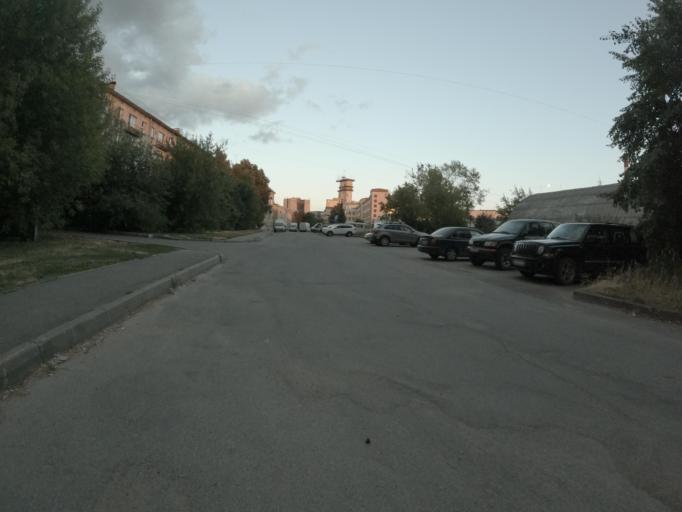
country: RU
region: St.-Petersburg
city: Centralniy
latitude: 59.9132
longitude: 30.3379
